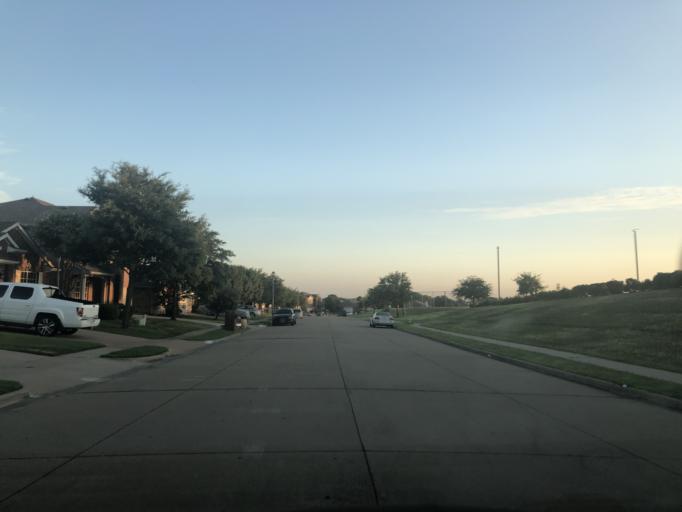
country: US
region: Texas
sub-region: Dallas County
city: Cedar Hill
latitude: 32.6524
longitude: -96.9756
